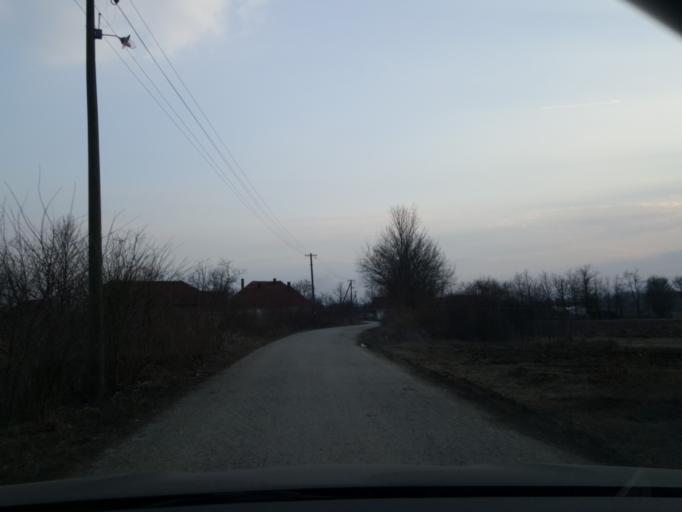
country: RS
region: Central Serbia
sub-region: Nisavski Okrug
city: Aleksinac
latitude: 43.5842
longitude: 21.6475
